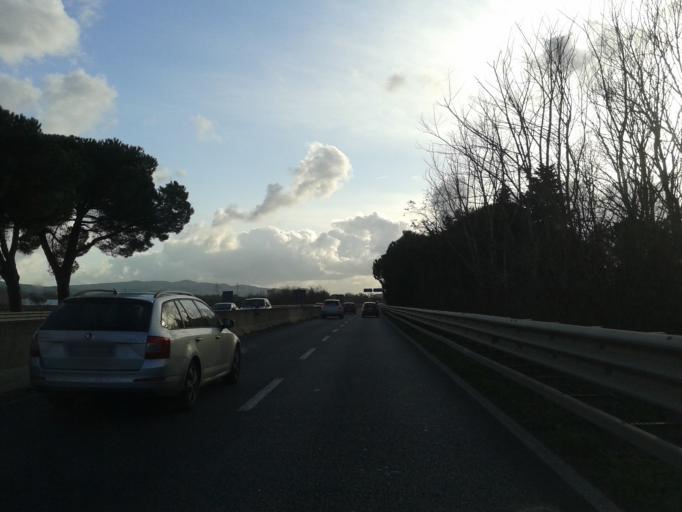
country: IT
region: Tuscany
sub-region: Provincia di Livorno
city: Livorno
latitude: 43.5606
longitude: 10.3456
